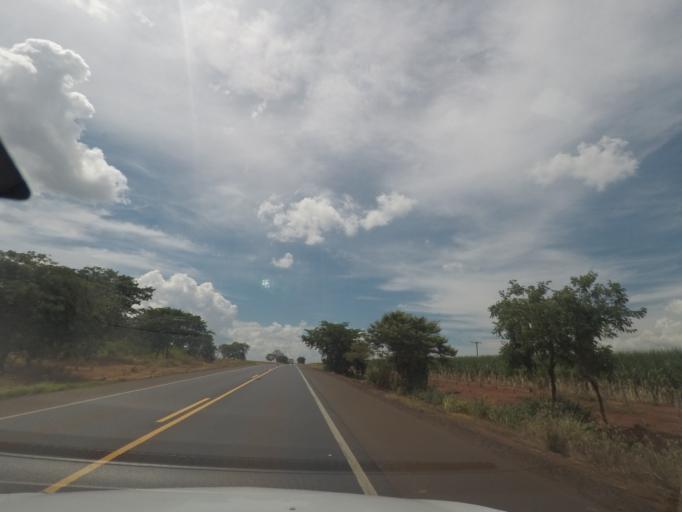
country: BR
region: Sao Paulo
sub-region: Barretos
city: Barretos
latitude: -20.2827
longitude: -48.6709
